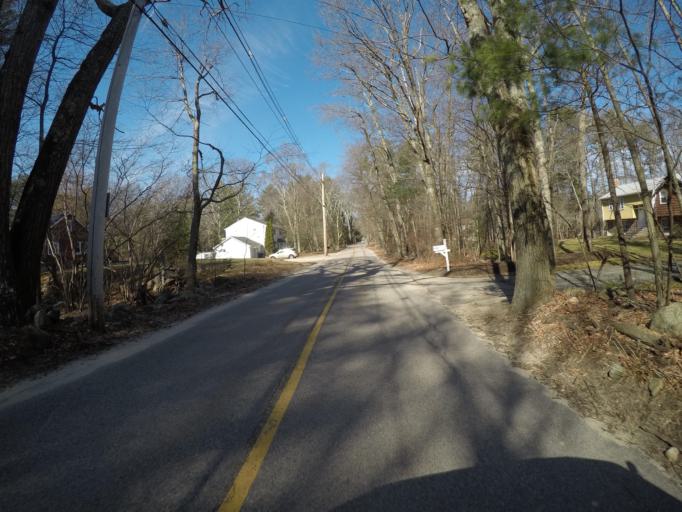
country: US
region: Massachusetts
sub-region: Norfolk County
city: Sharon
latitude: 42.0949
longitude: -71.1573
